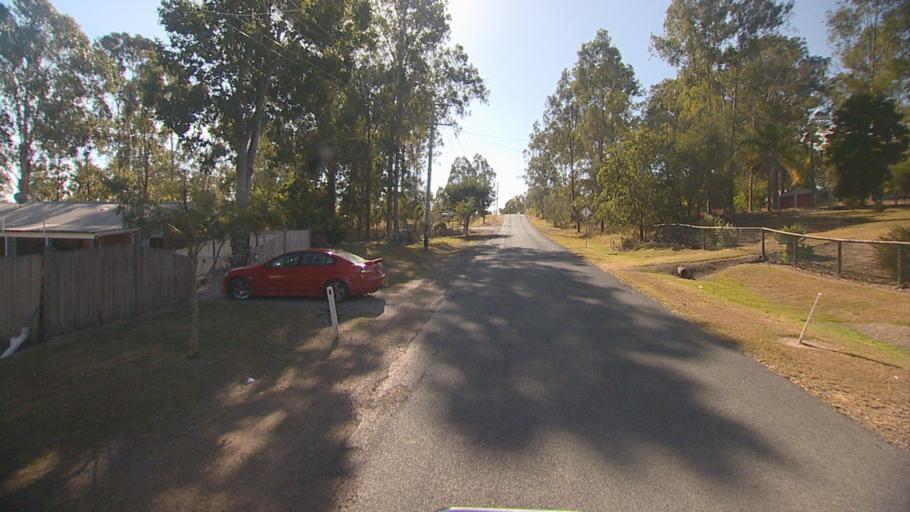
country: AU
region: Queensland
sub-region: Logan
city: Cedar Vale
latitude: -27.8565
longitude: 152.9843
